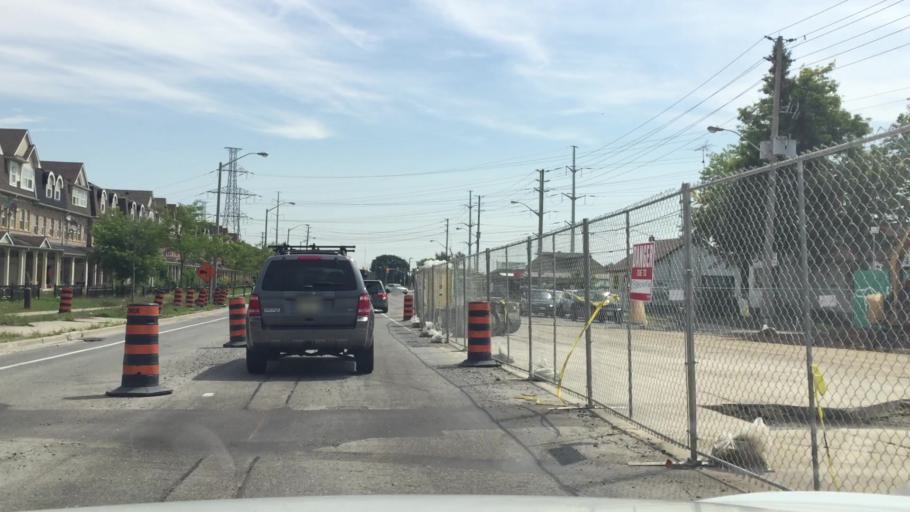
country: CA
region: Ontario
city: Scarborough
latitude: 43.8057
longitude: -79.1833
